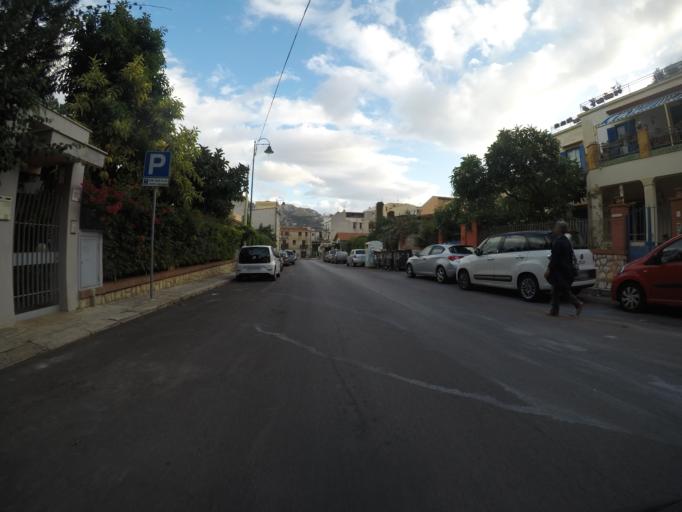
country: IT
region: Sicily
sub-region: Palermo
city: Palermo
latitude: 38.2093
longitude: 13.3271
